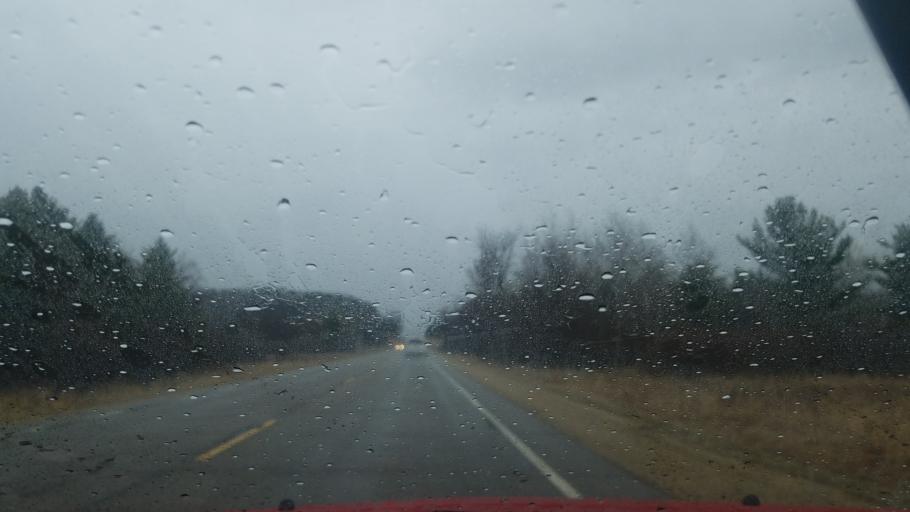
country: US
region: Wisconsin
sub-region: Dunn County
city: Tainter Lake
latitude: 44.9844
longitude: -91.8944
